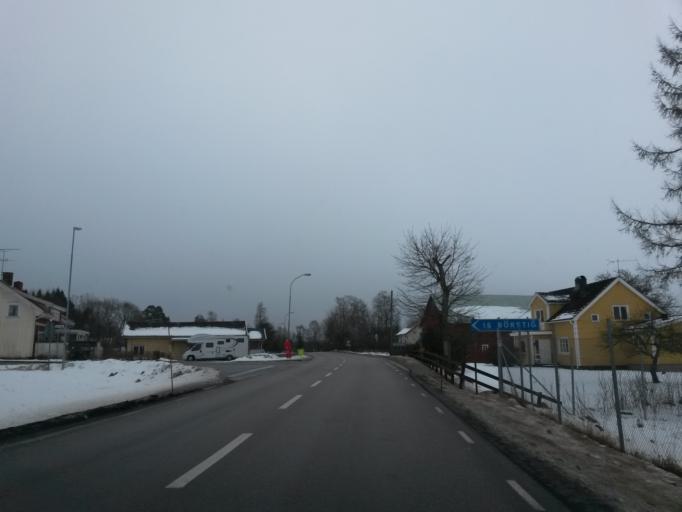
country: SE
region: Vaestra Goetaland
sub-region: Ulricehamns Kommun
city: Ulricehamn
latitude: 57.9006
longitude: 13.3466
